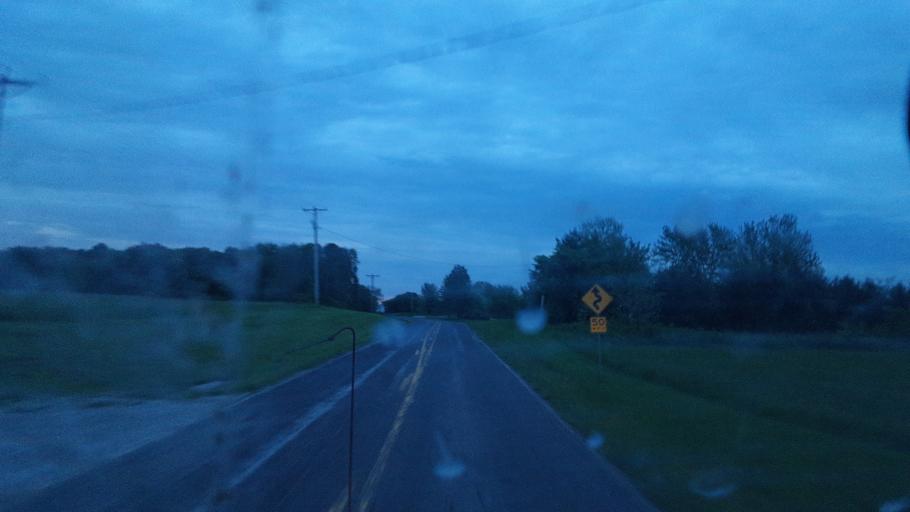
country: US
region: Missouri
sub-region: Clark County
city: Kahoka
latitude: 40.4355
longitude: -91.5912
